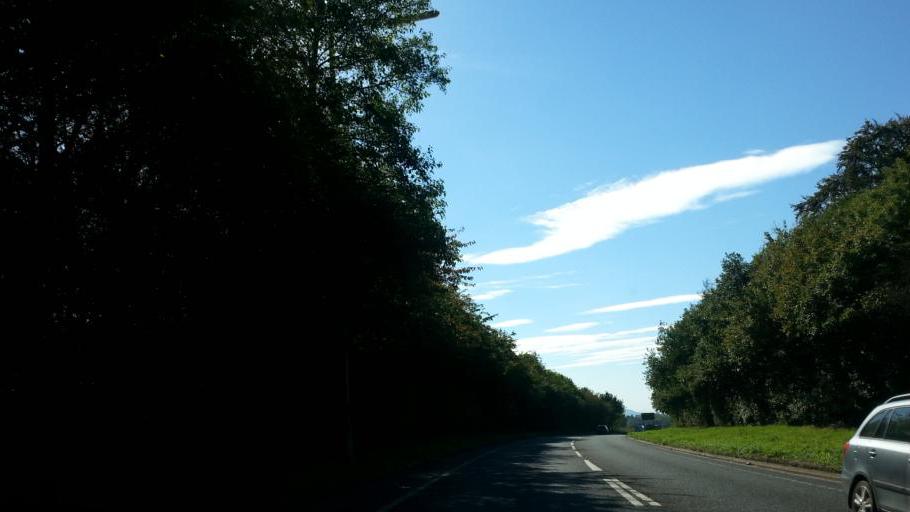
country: GB
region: England
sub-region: Telford and Wrekin
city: Newport
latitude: 52.7550
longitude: -2.3748
